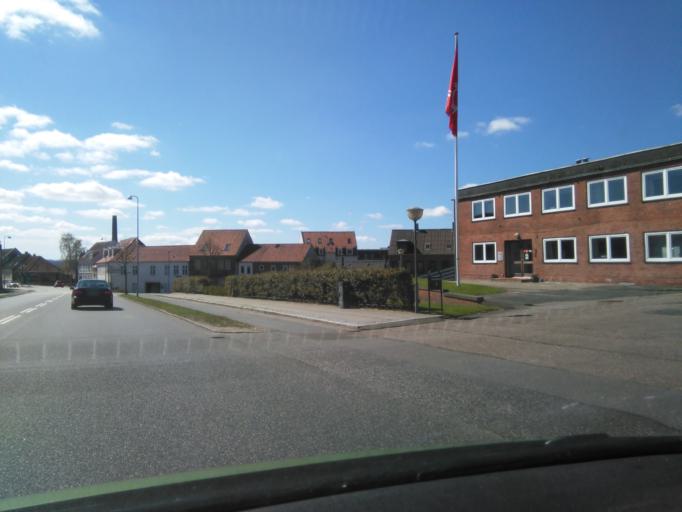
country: DK
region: Central Jutland
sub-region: Horsens Kommune
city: Horsens
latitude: 55.8710
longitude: 9.8441
